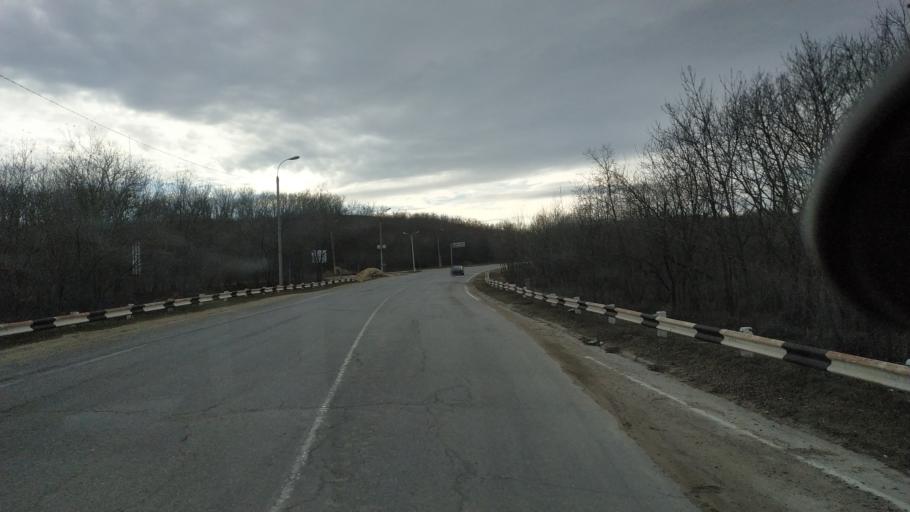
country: MD
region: Chisinau
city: Vadul lui Voda
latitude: 47.0840
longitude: 29.0875
